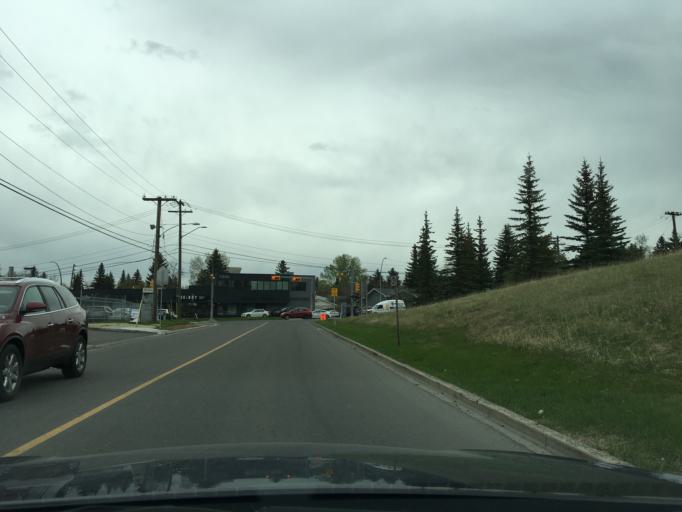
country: CA
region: Alberta
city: Calgary
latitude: 50.9880
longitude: -114.0647
